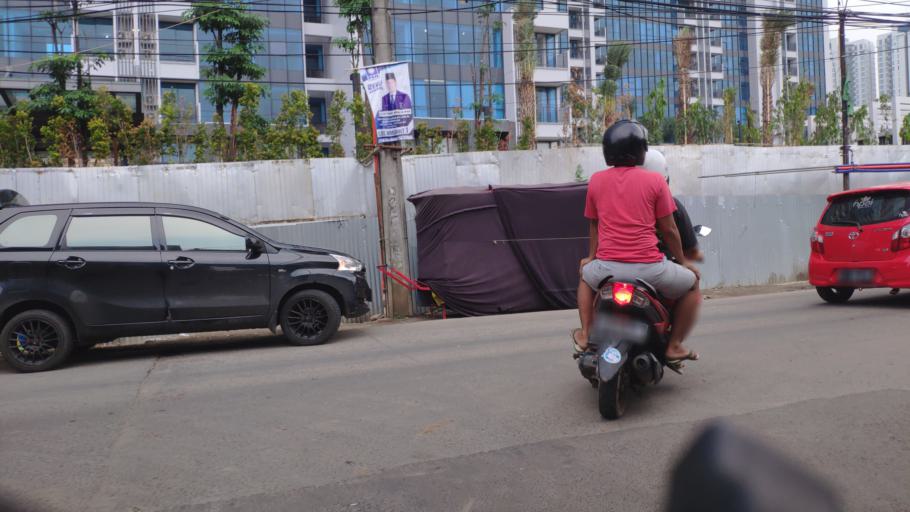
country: ID
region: Jakarta Raya
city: Jakarta
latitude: -6.2214
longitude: 106.8420
